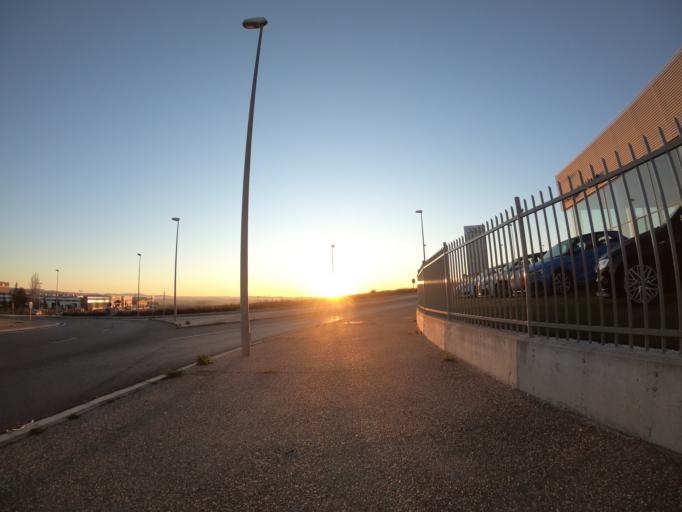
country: ES
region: Basque Country
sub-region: Provincia de Alava
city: Oyon
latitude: 42.4878
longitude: -2.4265
